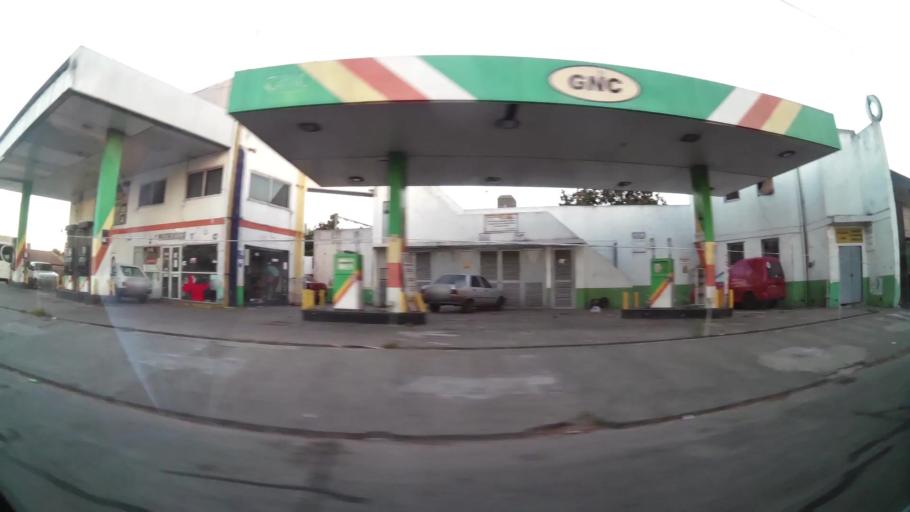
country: AR
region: Buenos Aires F.D.
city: Villa Lugano
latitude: -34.6691
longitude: -58.4747
